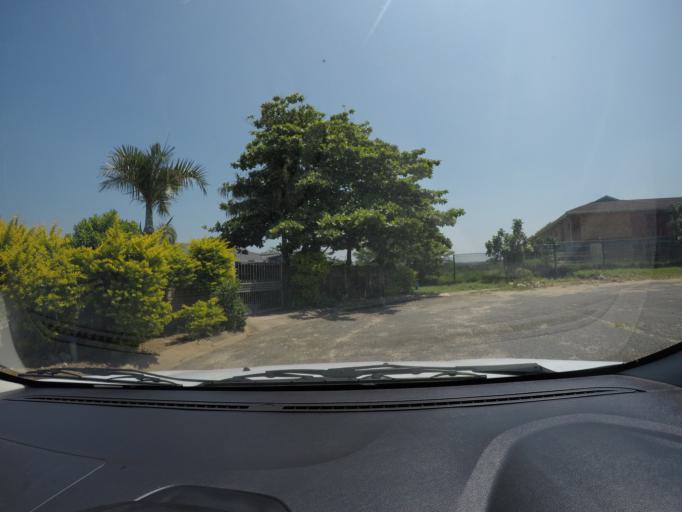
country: ZA
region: KwaZulu-Natal
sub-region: uThungulu District Municipality
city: eSikhawini
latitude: -28.8684
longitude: 31.9208
